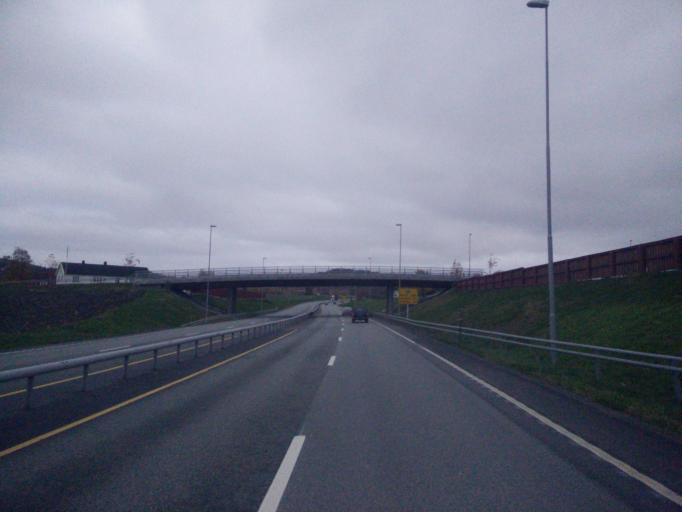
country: NO
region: Nord-Trondelag
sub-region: Stjordal
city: Stjordal
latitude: 63.4819
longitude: 10.8955
